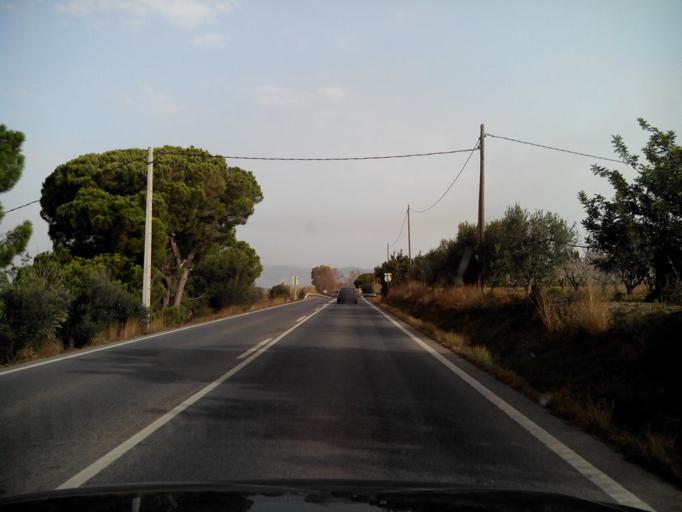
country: ES
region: Catalonia
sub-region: Provincia de Tarragona
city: Cambrils
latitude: 41.0965
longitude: 1.0827
